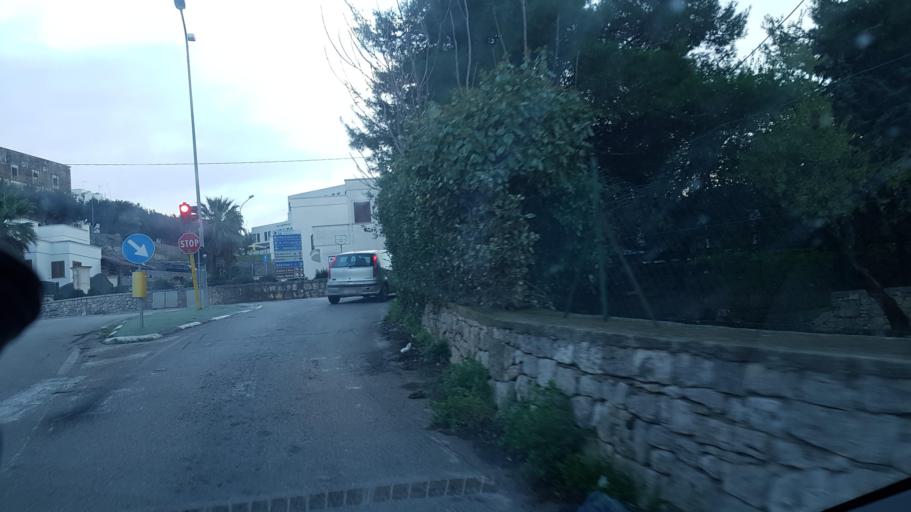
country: IT
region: Apulia
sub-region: Provincia di Brindisi
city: Ceglie Messapica
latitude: 40.6493
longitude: 17.5192
